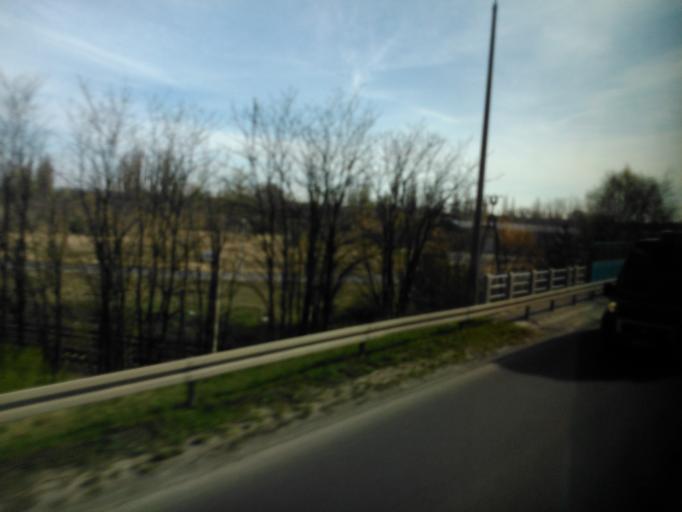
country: PL
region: Kujawsko-Pomorskie
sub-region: Torun
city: Torun
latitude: 52.9917
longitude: 18.6582
